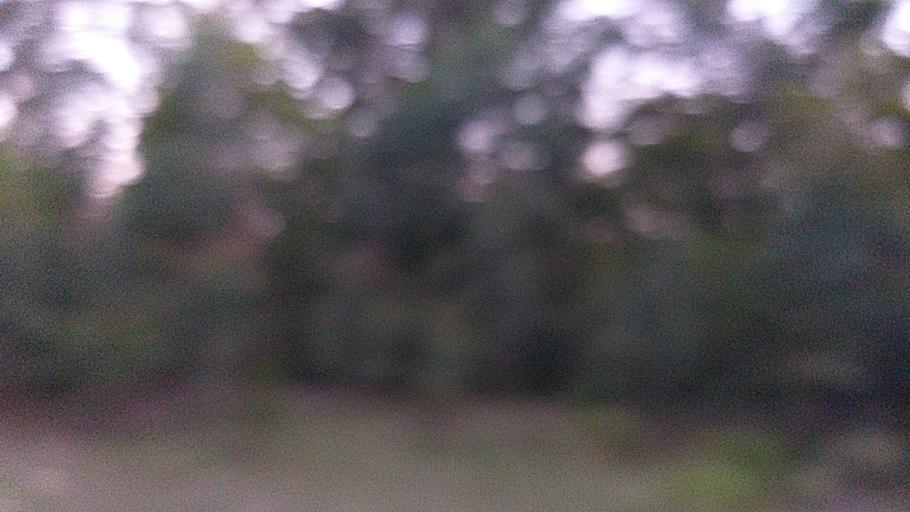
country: AU
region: New South Wales
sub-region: Wollongong
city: Helensburgh
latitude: -34.1652
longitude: 151.0031
